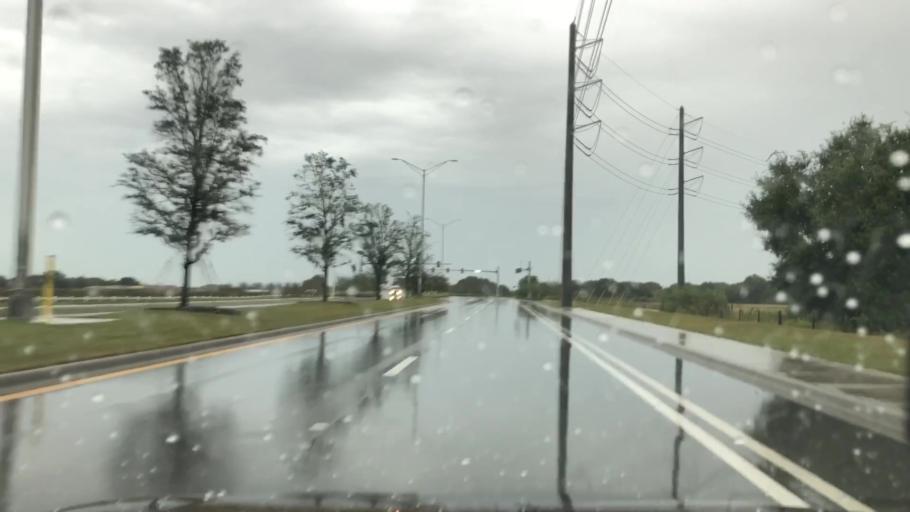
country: US
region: Florida
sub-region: Sarasota County
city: Fruitville
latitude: 27.3588
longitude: -82.3872
